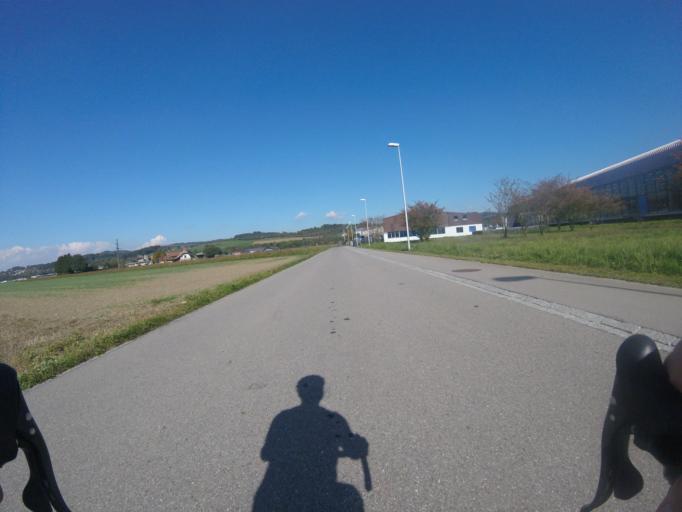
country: CH
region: Bern
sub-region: Bern-Mittelland District
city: Belp
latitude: 46.9029
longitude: 7.5034
